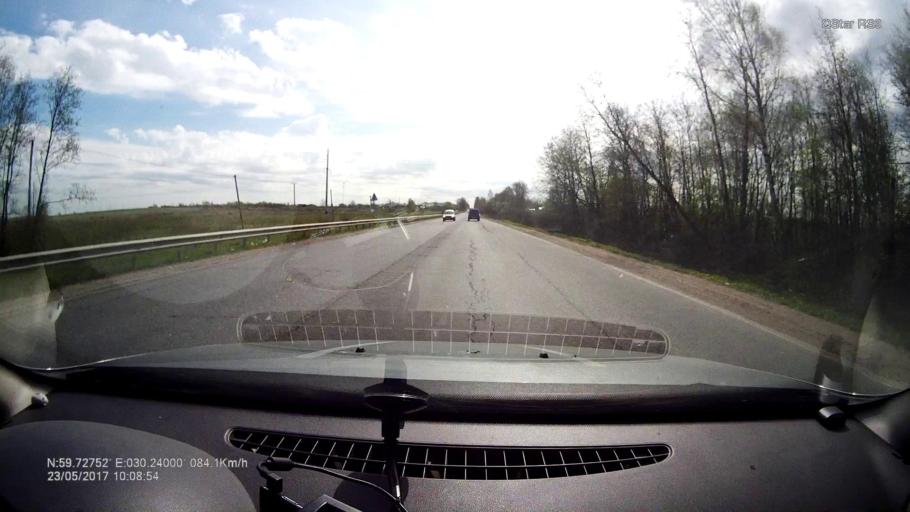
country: RU
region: St.-Petersburg
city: Aleksandrovskaya
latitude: 59.7275
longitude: 30.2402
